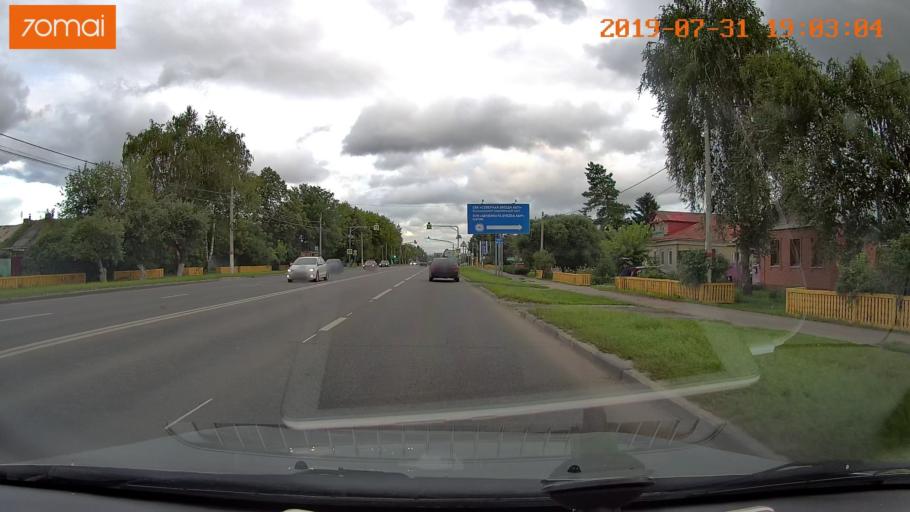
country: RU
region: Moskovskaya
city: Raduzhnyy
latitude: 55.1169
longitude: 38.7360
